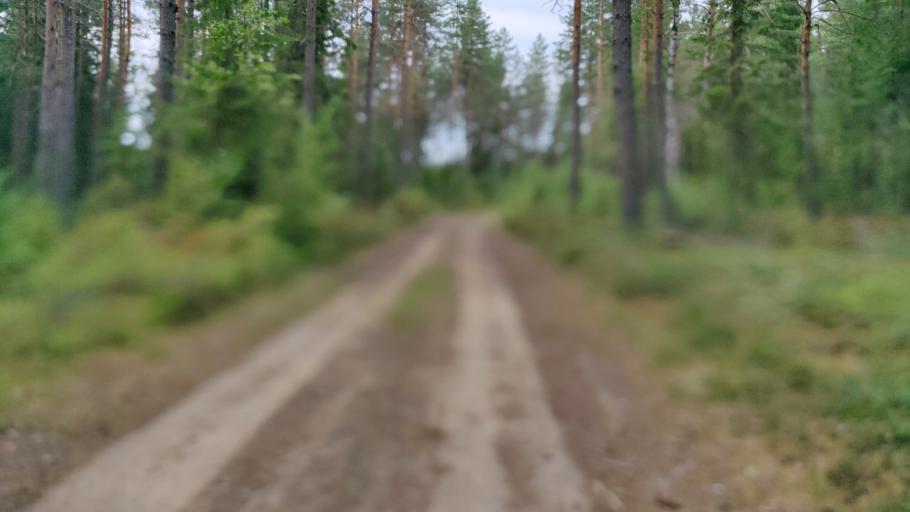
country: SE
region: Vaermland
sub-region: Hagfors Kommun
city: Hagfors
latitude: 60.0147
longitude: 13.5606
